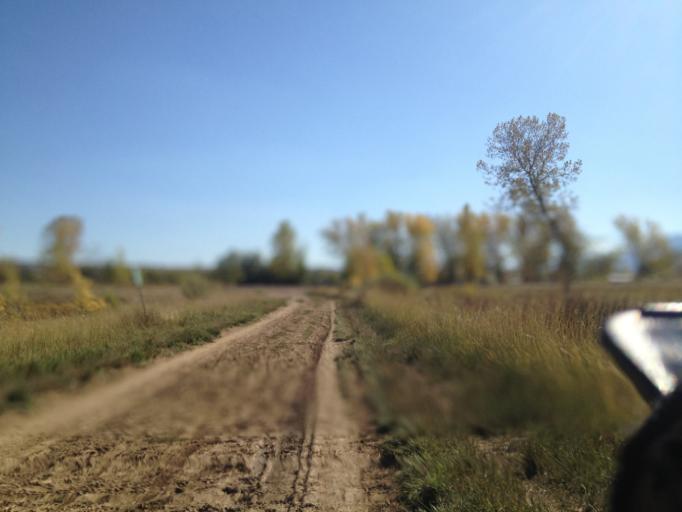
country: US
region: Colorado
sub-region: Boulder County
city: Boulder
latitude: 39.9728
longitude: -105.2341
